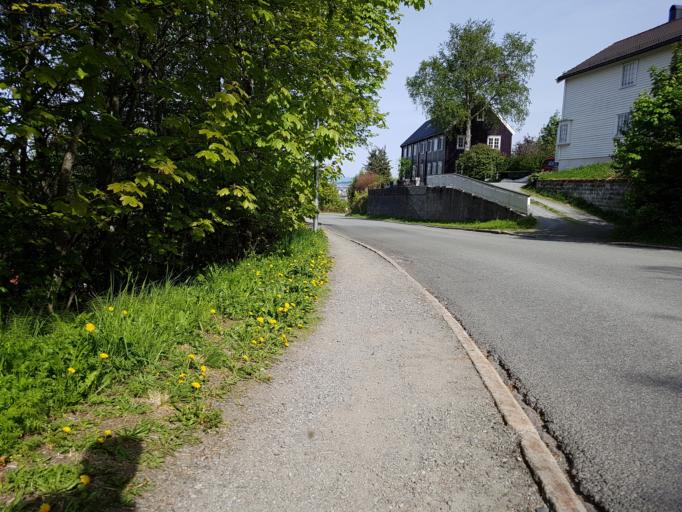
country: NO
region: Sor-Trondelag
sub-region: Trondheim
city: Trondheim
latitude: 63.4290
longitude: 10.3565
